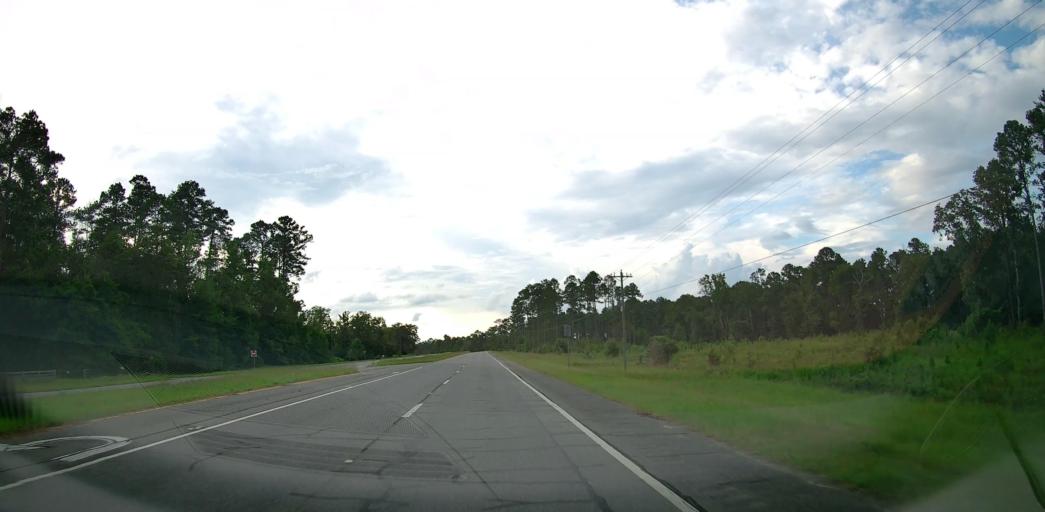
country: US
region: Georgia
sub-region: Pulaski County
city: Hawkinsville
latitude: 32.2652
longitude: -83.4105
